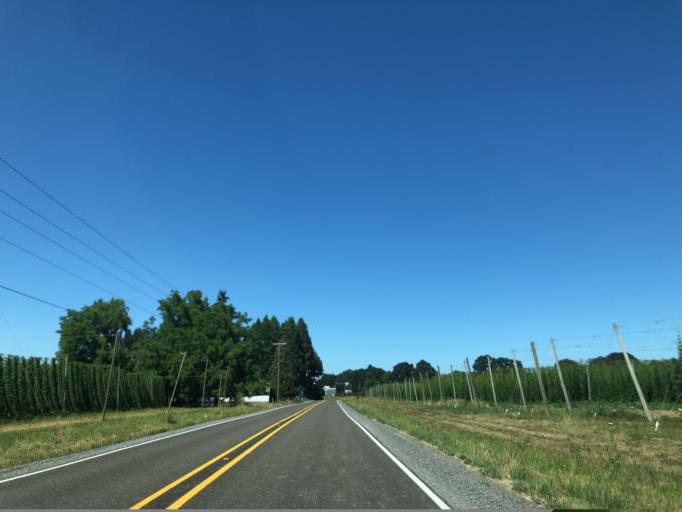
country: US
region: Oregon
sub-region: Marion County
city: Silverton
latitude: 45.0277
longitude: -122.7647
